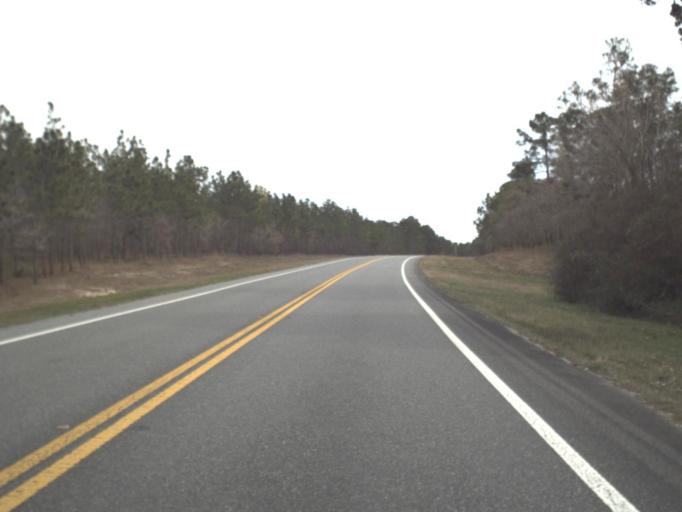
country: US
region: Florida
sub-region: Wakulla County
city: Crawfordville
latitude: 30.2979
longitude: -84.4138
